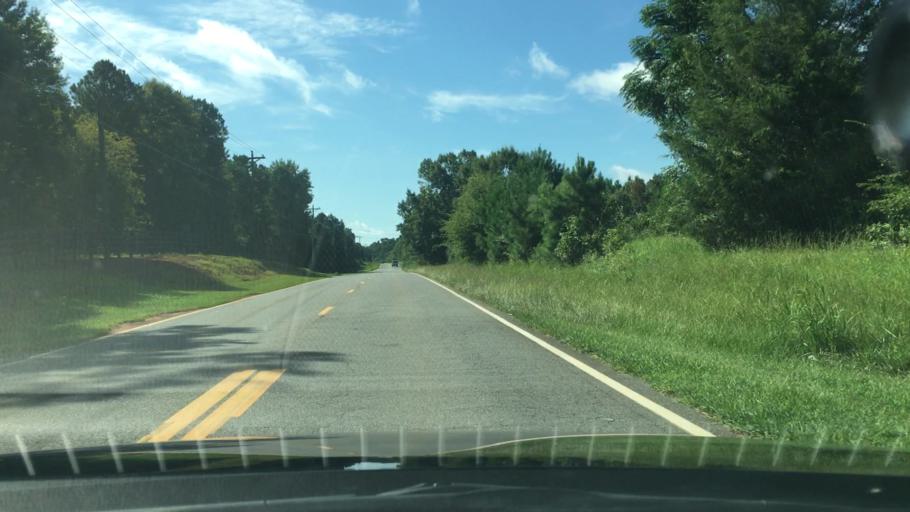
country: US
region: Georgia
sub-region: Putnam County
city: Jefferson
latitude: 33.4487
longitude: -83.2963
